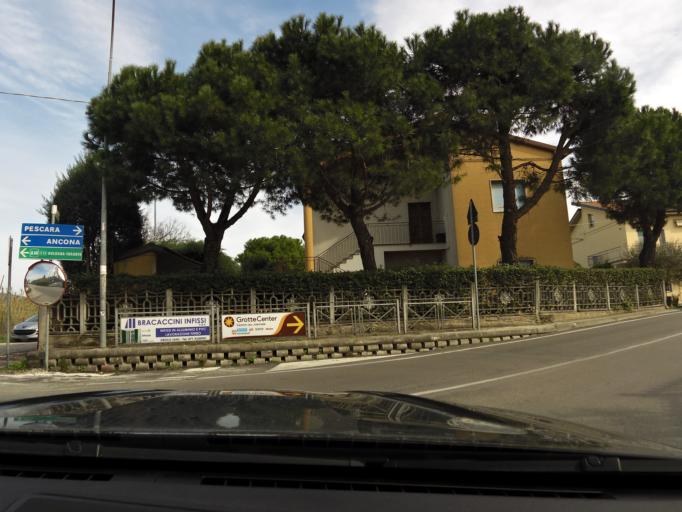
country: IT
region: The Marches
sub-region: Provincia di Ancona
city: San Biagio
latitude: 43.5281
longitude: 13.5214
